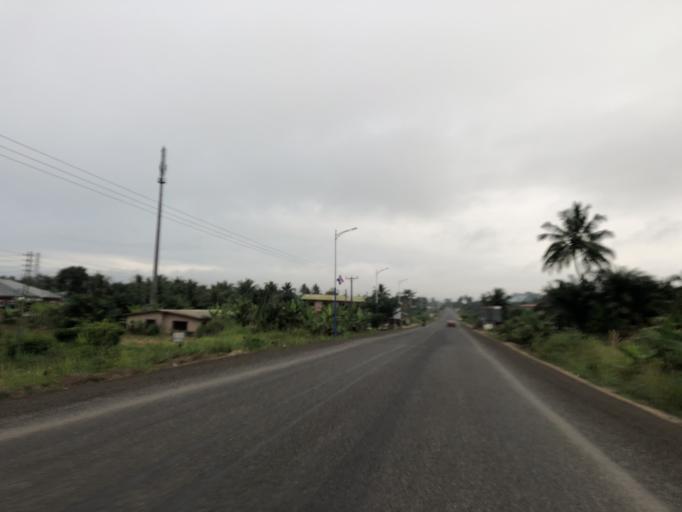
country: GH
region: Eastern
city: Koforidua
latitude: 6.1972
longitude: -0.3628
